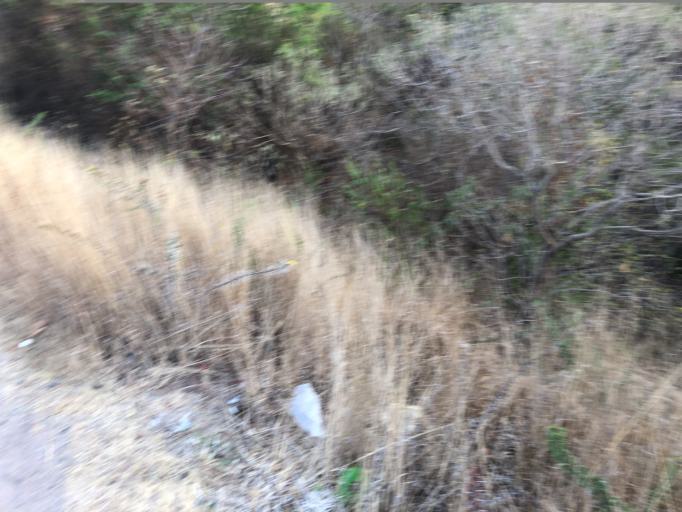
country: MX
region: Oaxaca
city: Ciudad de Huajuapam de Leon
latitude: 17.8372
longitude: -97.7916
